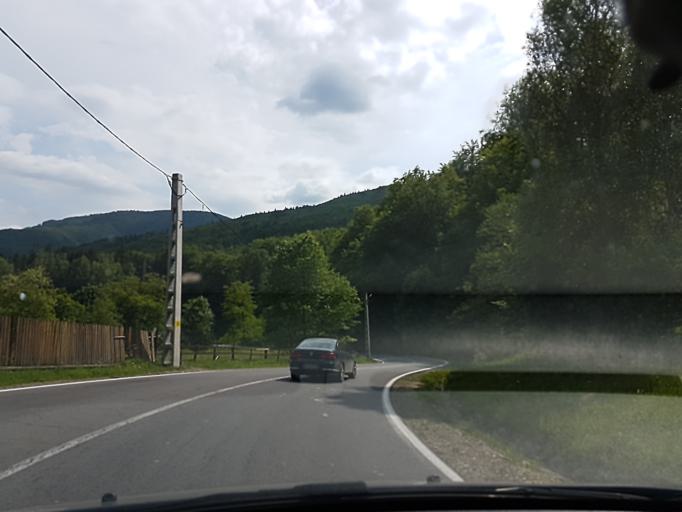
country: RO
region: Prahova
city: Maneciu
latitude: 45.3598
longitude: 25.9417
